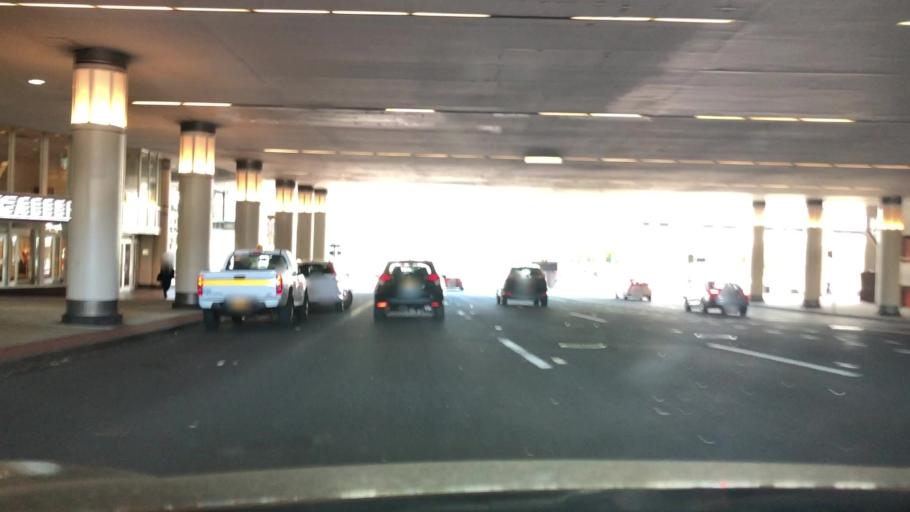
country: US
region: New York
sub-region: Westchester County
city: White Plains
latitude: 41.0316
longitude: -73.7701
